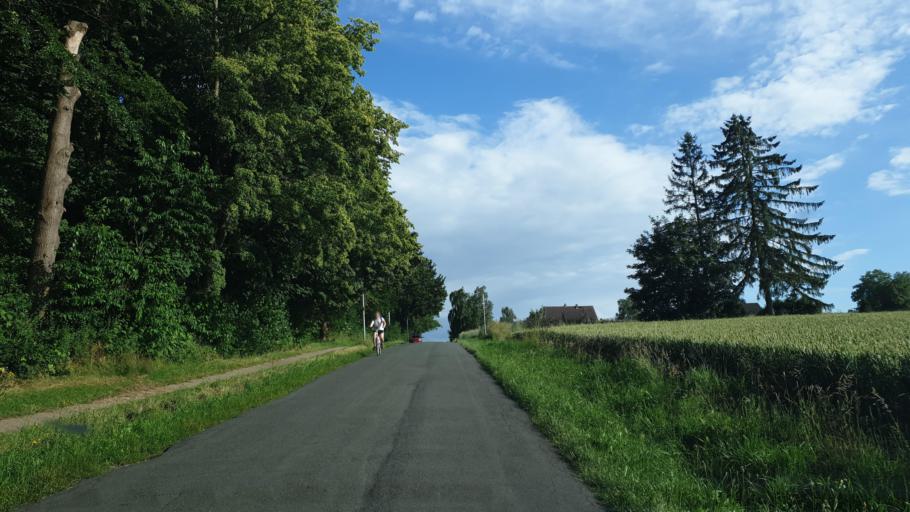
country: DE
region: North Rhine-Westphalia
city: Bad Oeynhausen
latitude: 52.1835
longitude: 8.7938
